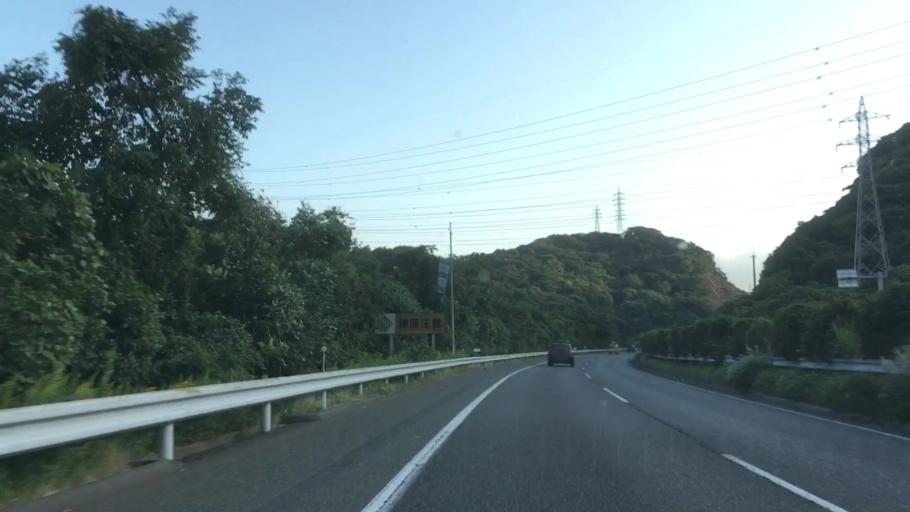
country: JP
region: Yamaguchi
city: Shimonoseki
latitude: 33.8960
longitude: 130.9725
